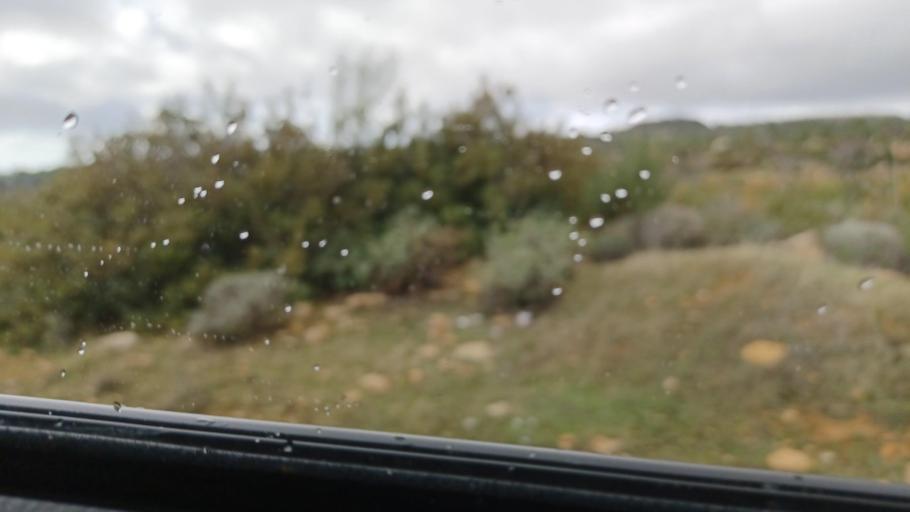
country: CY
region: Limassol
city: Sotira
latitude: 34.7416
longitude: 32.8591
